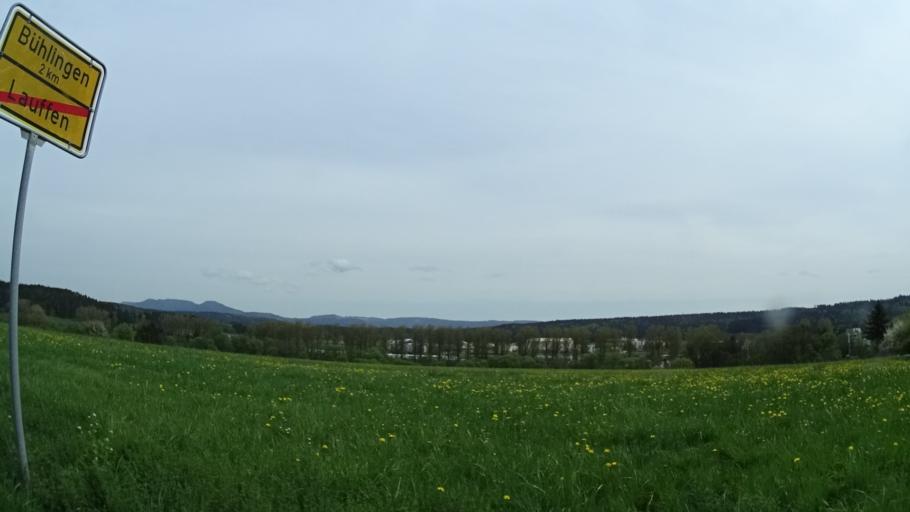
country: DE
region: Baden-Wuerttemberg
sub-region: Freiburg Region
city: Deisslingen
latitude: 48.1302
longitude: 8.6274
